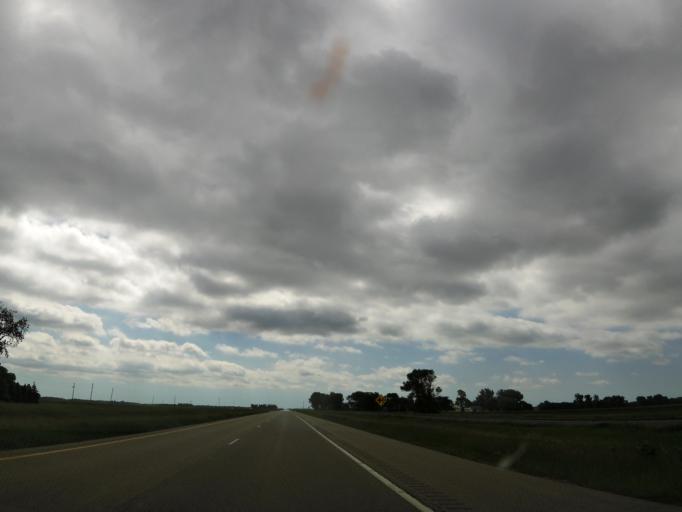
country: US
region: Minnesota
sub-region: Polk County
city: East Grand Forks
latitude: 47.8793
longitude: -96.9155
